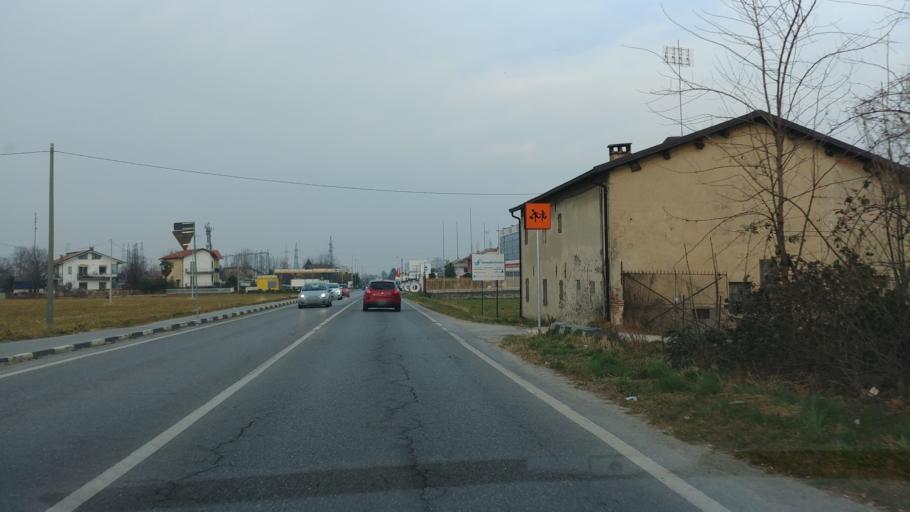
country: IT
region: Piedmont
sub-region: Provincia di Cuneo
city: Borgo San Dalmazzo
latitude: 44.3546
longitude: 7.5120
